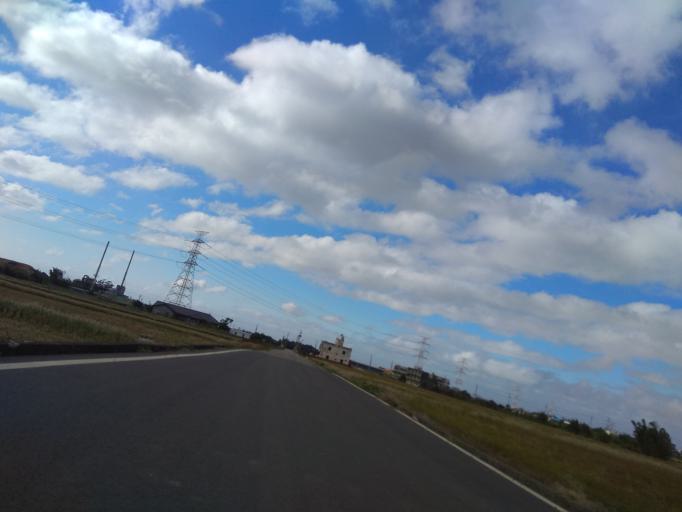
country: TW
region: Taiwan
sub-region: Hsinchu
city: Zhubei
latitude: 24.9716
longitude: 121.0790
